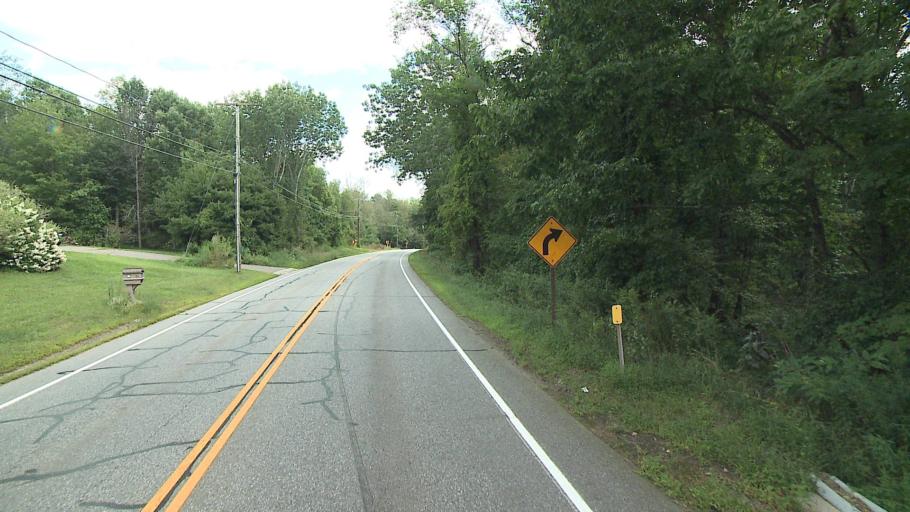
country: US
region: Connecticut
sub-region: Tolland County
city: Crystal Lake
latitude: 41.9191
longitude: -72.4217
